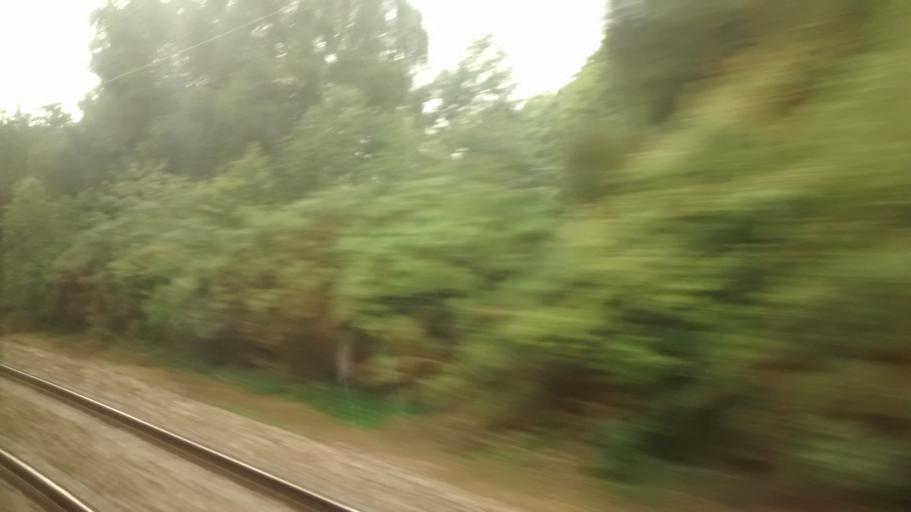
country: FR
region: Pays de la Loire
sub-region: Departement de la Sarthe
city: Vibraye
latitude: 48.0766
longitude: 0.6860
